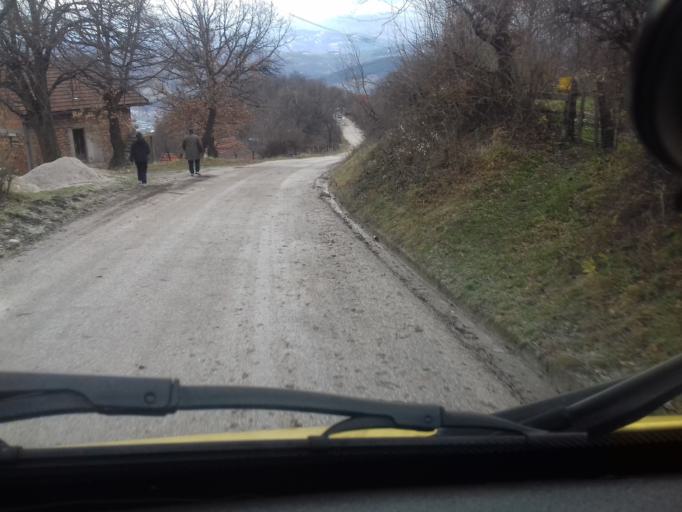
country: BA
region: Federation of Bosnia and Herzegovina
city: Zenica
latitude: 44.2260
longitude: 17.9436
